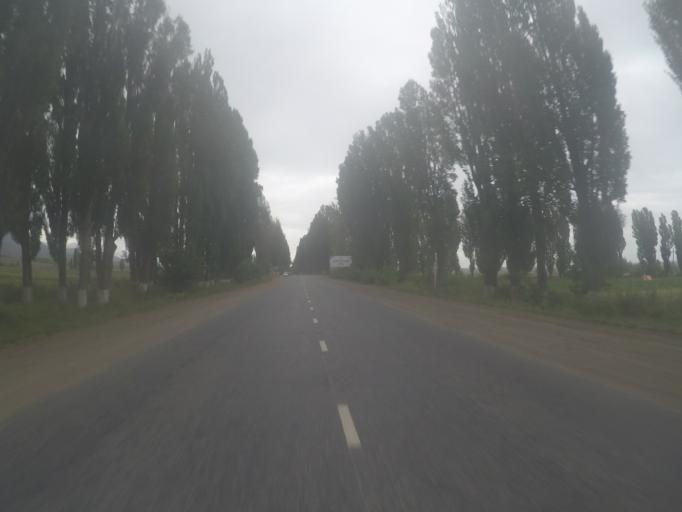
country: KG
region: Ysyk-Koel
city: Cholpon-Ata
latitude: 42.6925
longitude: 77.3773
